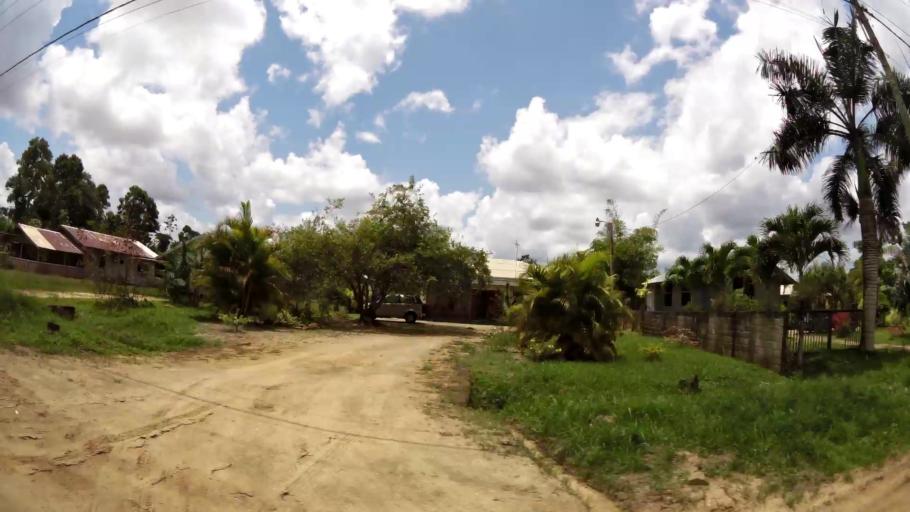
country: SR
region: Paramaribo
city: Paramaribo
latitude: 5.7988
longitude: -55.1376
